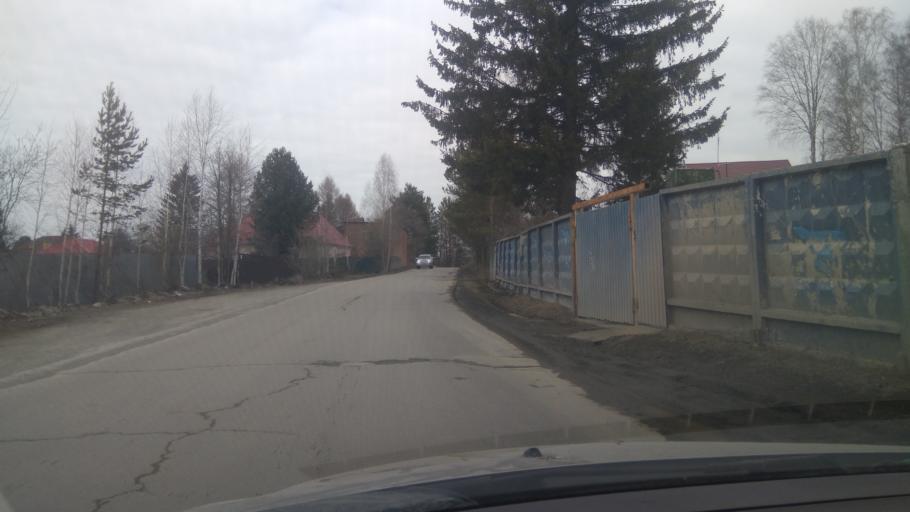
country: RU
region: Sverdlovsk
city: Severka
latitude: 56.8458
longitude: 60.3833
